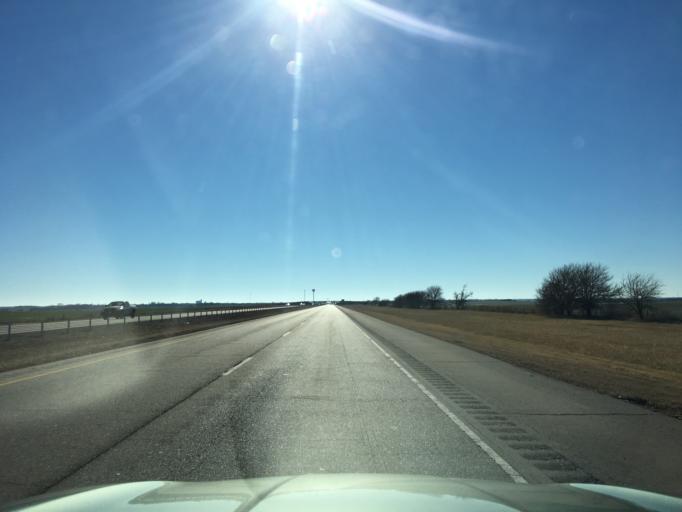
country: US
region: Oklahoma
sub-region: Kay County
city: Blackwell
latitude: 36.9648
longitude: -97.3458
